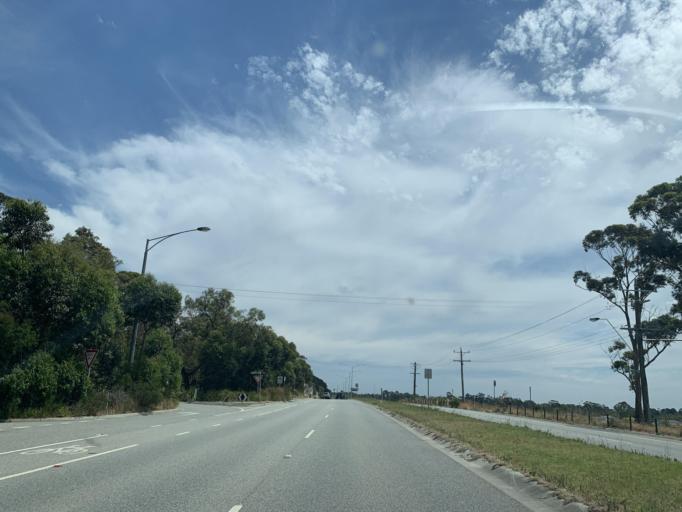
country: AU
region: Victoria
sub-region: Casey
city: Cranbourne South
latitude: -38.1296
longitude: 145.2378
